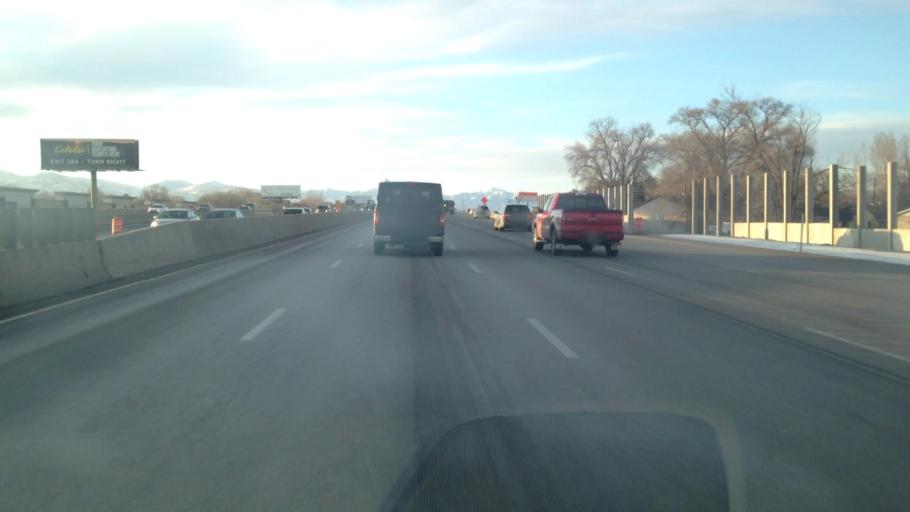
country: US
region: Utah
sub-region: Utah County
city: Lehi
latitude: 40.3974
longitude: -111.8435
